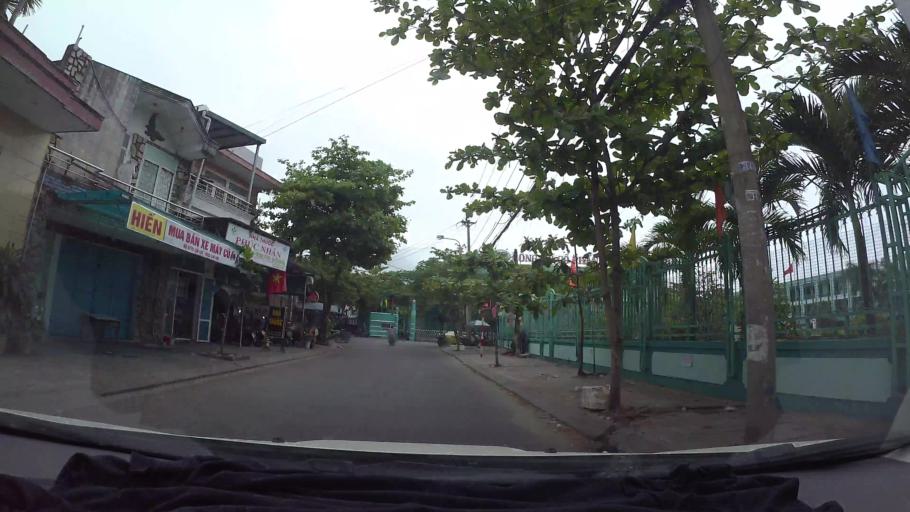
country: VN
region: Da Nang
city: Thanh Khe
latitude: 16.0668
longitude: 108.1800
